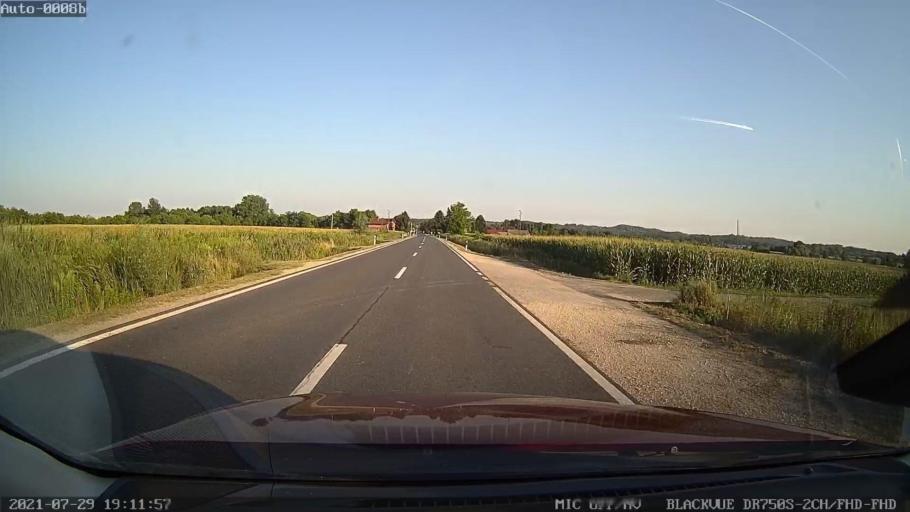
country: HR
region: Varazdinska
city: Jalzabet
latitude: 46.2720
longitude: 16.5131
